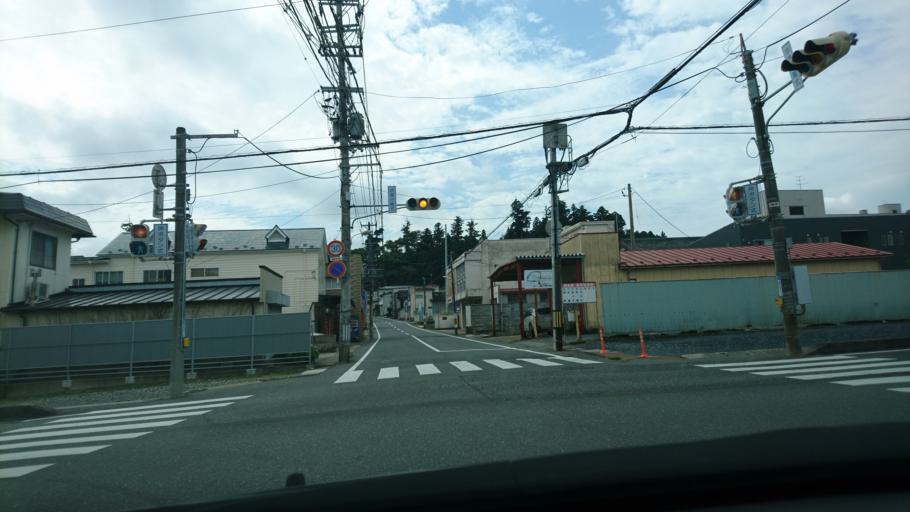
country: JP
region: Miyagi
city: Furukawa
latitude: 38.7331
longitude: 141.0188
